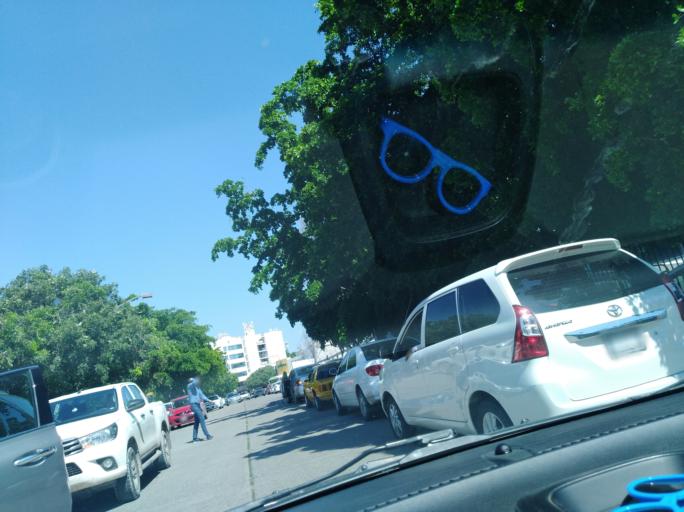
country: MX
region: Sinaloa
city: Culiacan
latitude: 24.7939
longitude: -107.4147
